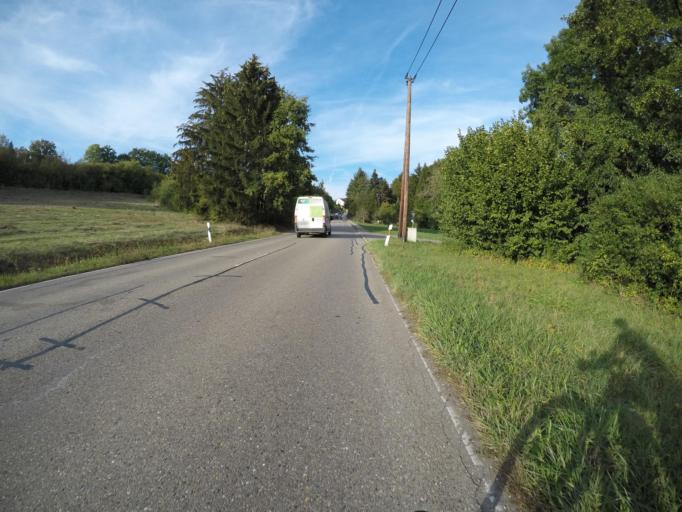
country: DE
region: Baden-Wuerttemberg
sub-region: Regierungsbezirk Stuttgart
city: Neuhausen auf den Fildern
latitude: 48.7053
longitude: 9.2892
